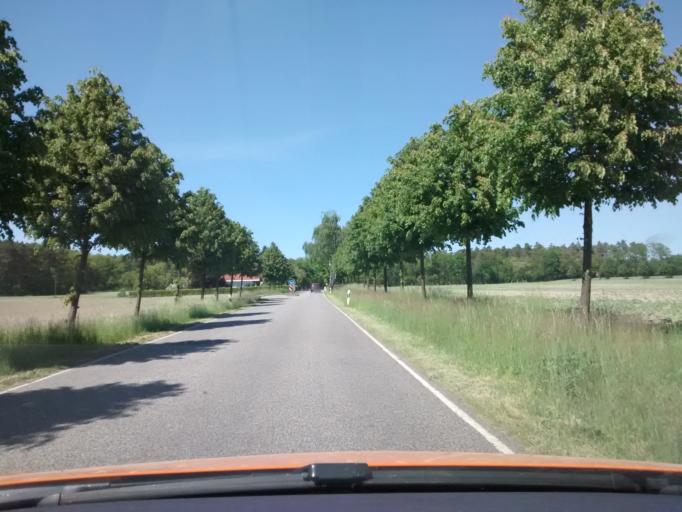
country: DE
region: Brandenburg
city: Reichenwalde
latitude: 52.2377
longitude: 13.9940
